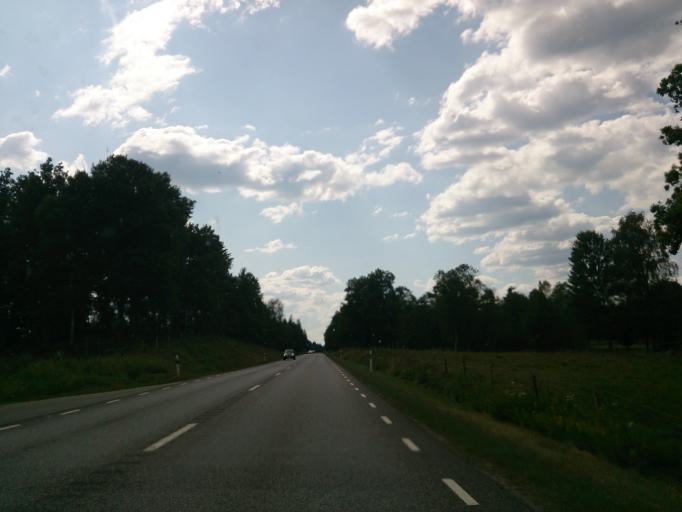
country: SE
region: Joenkoeping
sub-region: Gislaveds Kommun
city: Reftele
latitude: 57.1621
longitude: 13.5571
